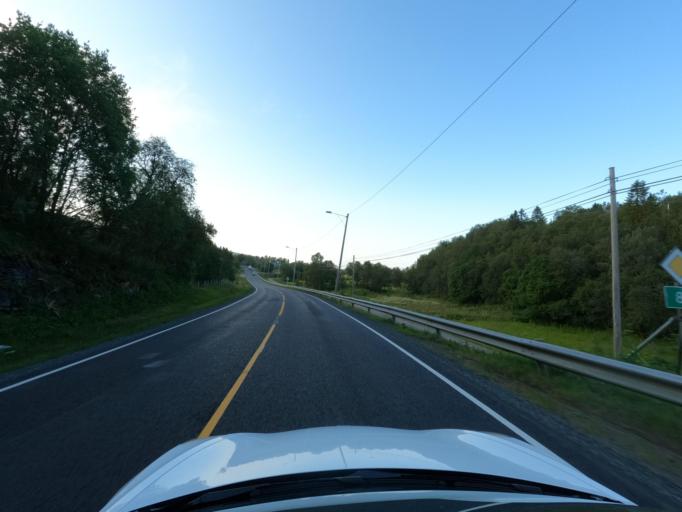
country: NO
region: Troms
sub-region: Skanland
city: Evenskjer
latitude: 68.6662
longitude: 16.5757
